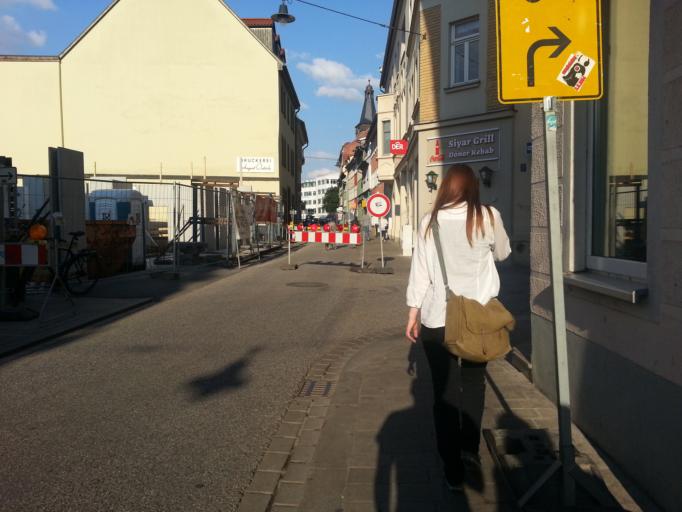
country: DE
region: Thuringia
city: Erfurt
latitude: 50.9784
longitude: 11.0327
